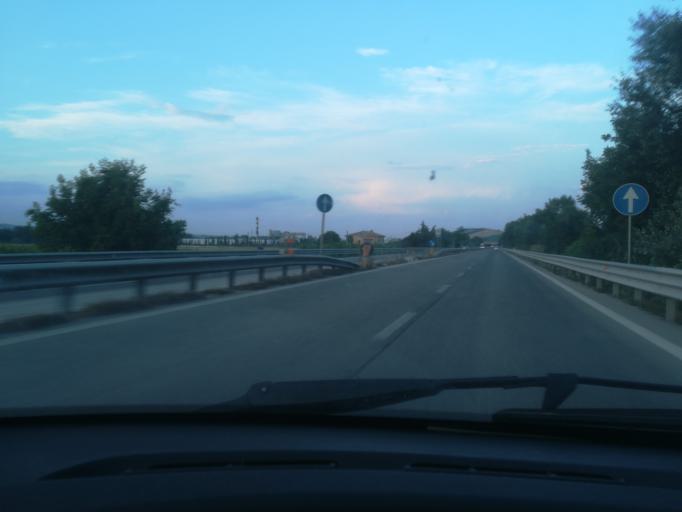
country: IT
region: The Marches
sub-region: Provincia di Macerata
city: Casette Verdini
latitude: 43.2352
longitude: 13.3805
